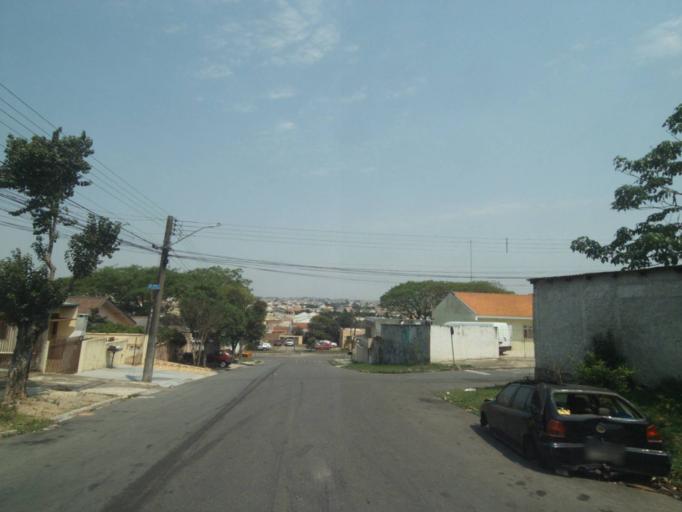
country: BR
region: Parana
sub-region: Sao Jose Dos Pinhais
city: Sao Jose dos Pinhais
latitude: -25.5332
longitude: -49.2496
